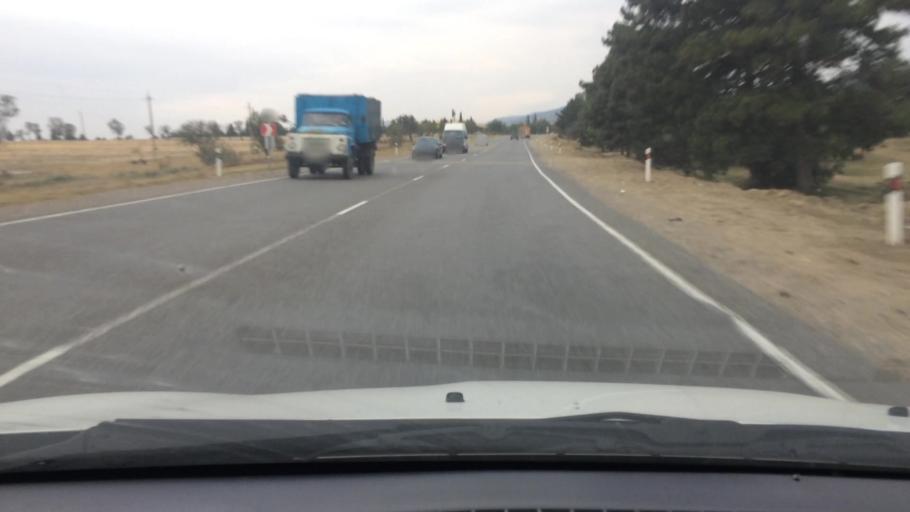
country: GE
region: T'bilisi
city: Tbilisi
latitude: 41.6385
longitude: 44.8746
